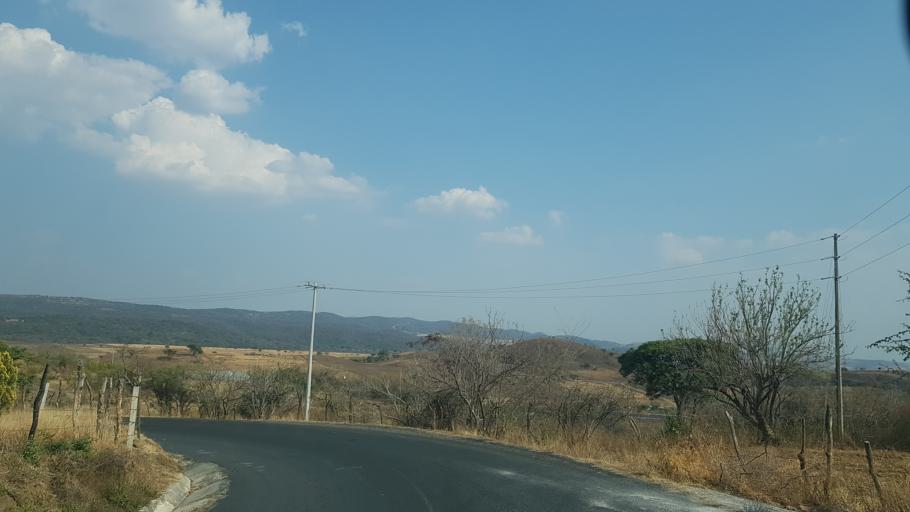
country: MX
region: Morelos
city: Tlacotepec
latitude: 18.8016
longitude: -98.7127
